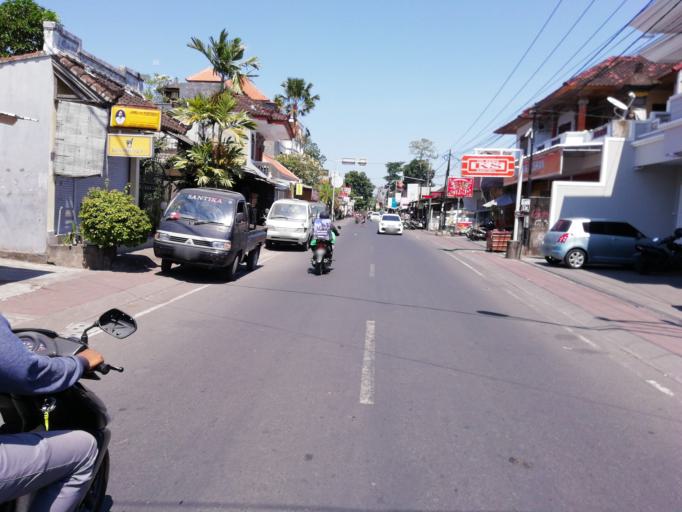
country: ID
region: Bali
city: Karyadharma
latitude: -8.6807
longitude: 115.2259
